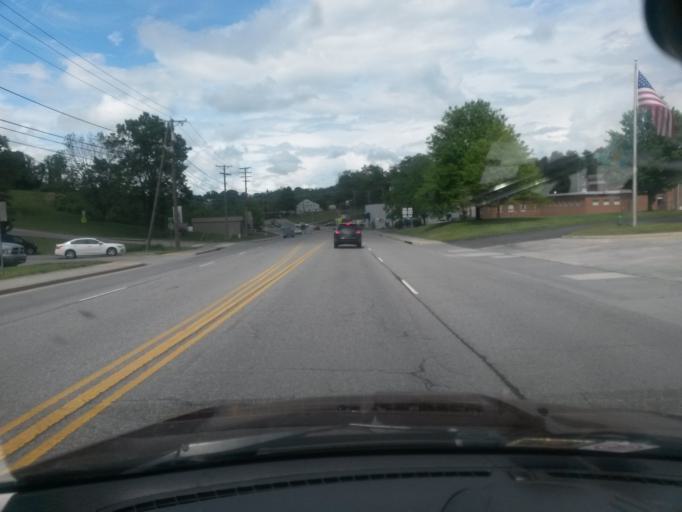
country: US
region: Virginia
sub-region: Montgomery County
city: Christiansburg
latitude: 37.1311
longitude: -80.4142
